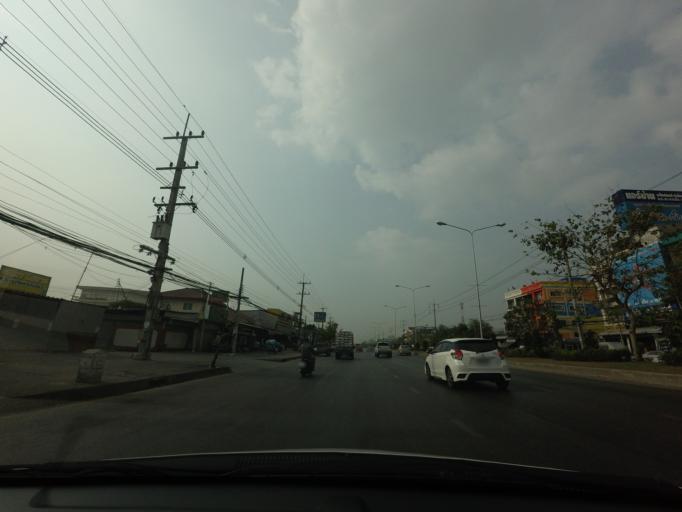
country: TH
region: Bangkok
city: Nong Khaem
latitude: 13.7404
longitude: 100.3295
